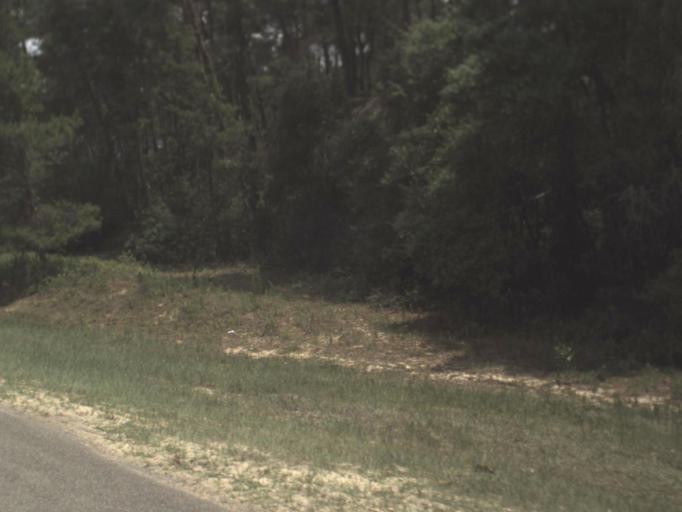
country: US
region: Florida
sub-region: Putnam County
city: Crescent City
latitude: 29.4013
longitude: -81.7367
